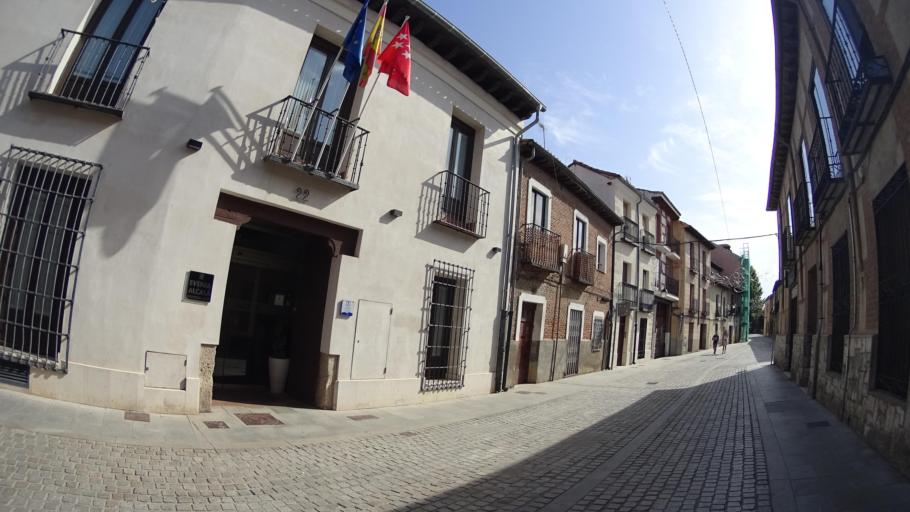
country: ES
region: Madrid
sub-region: Provincia de Madrid
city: Alcala de Henares
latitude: 40.4808
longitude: -3.3709
